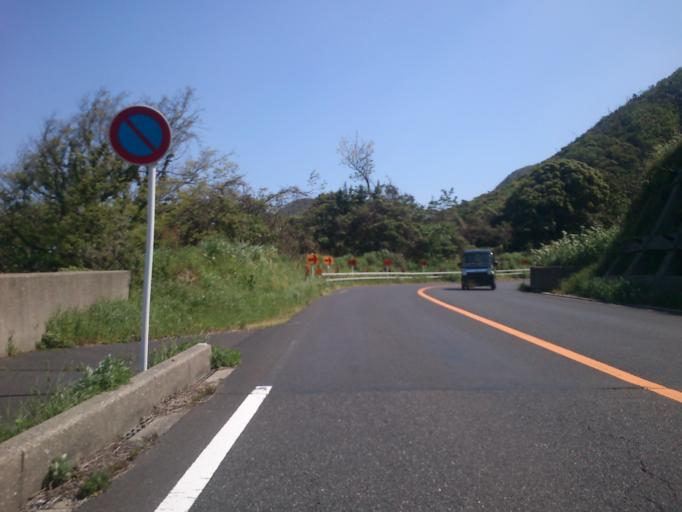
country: JP
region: Kyoto
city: Miyazu
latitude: 35.7461
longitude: 135.1277
